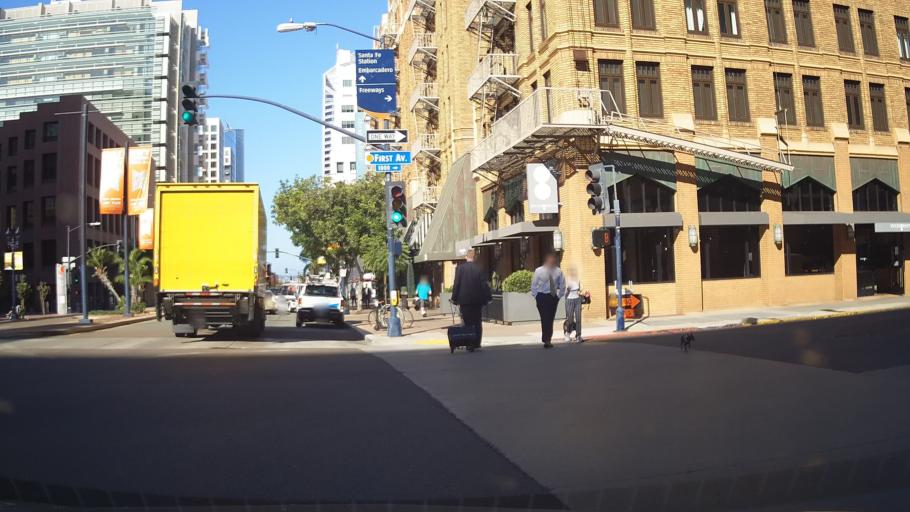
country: US
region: California
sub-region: San Diego County
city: San Diego
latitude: 32.7158
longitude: -117.1637
